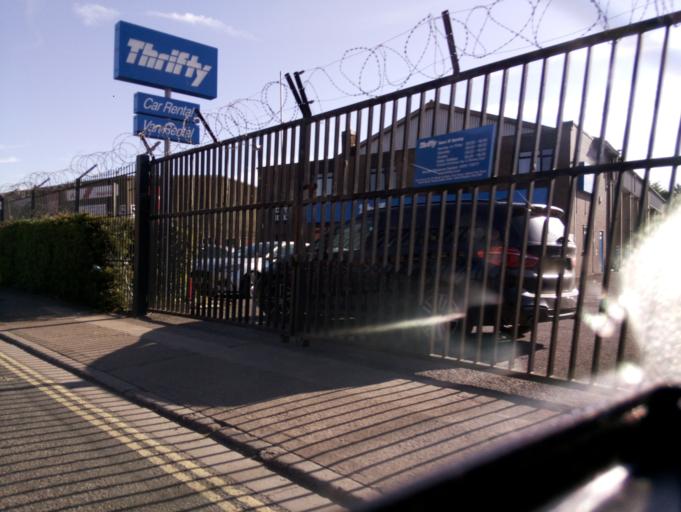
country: GB
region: England
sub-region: Bristol
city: Bristol
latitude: 51.4478
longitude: -2.5699
